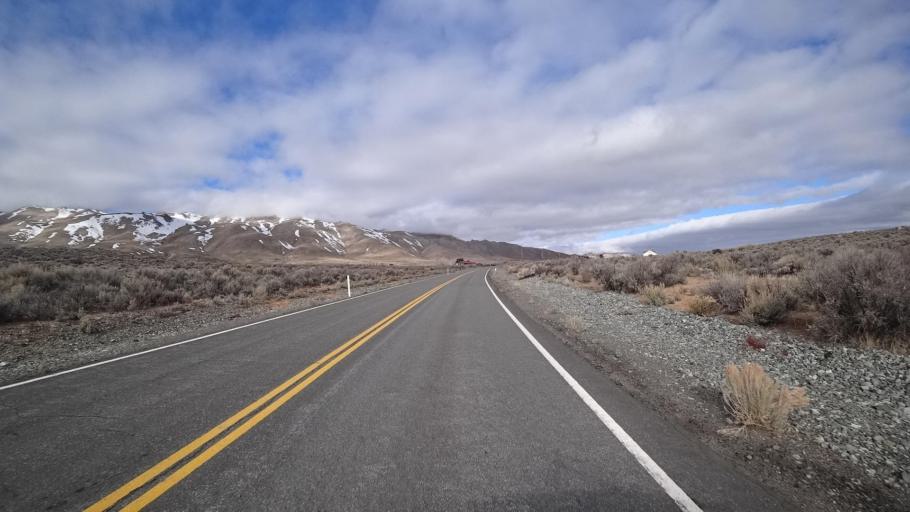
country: US
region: Nevada
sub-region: Washoe County
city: Cold Springs
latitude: 39.8674
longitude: -119.9484
